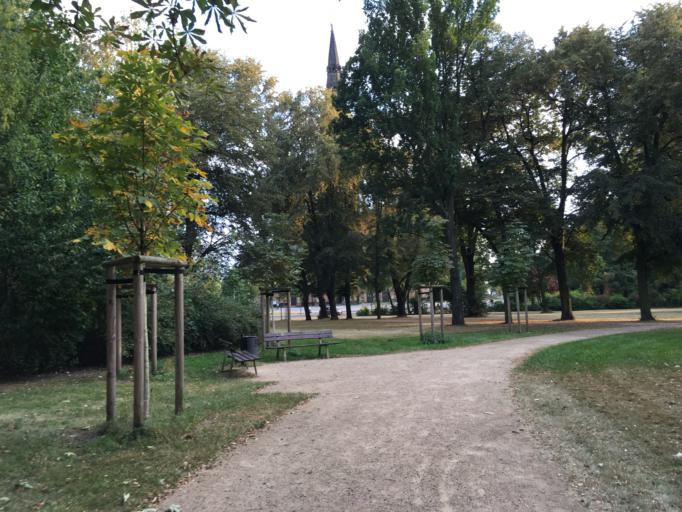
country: DE
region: Saxony
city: Albertstadt
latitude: 51.0762
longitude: 13.7599
